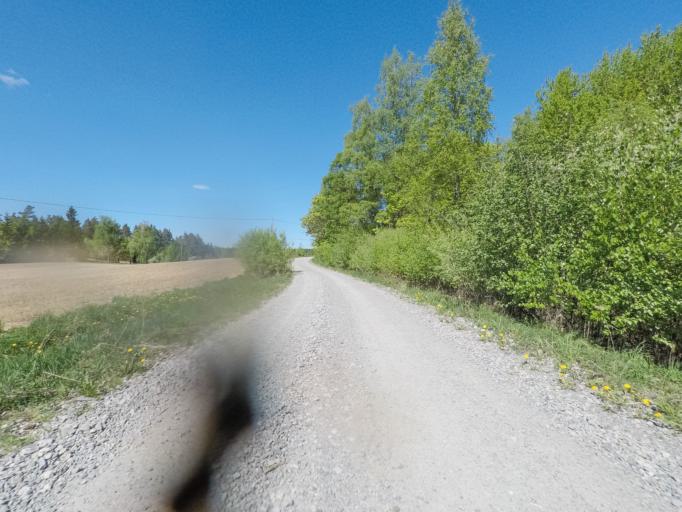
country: FI
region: Pirkanmaa
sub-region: Etelae-Pirkanmaa
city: Kylmaekoski
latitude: 61.1601
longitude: 23.7094
